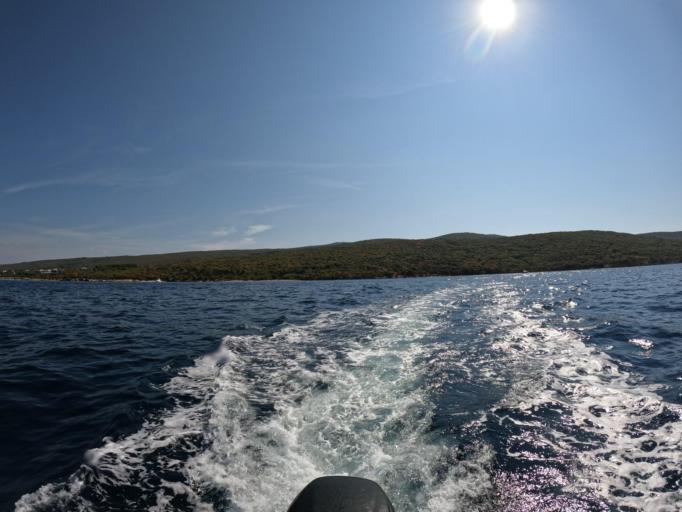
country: HR
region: Primorsko-Goranska
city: Punat
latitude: 45.0014
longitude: 14.6208
